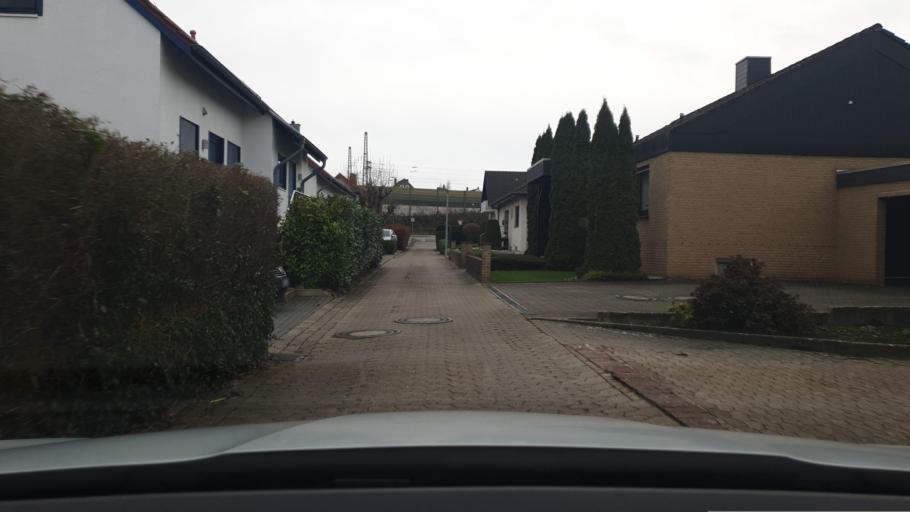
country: DE
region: North Rhine-Westphalia
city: Bad Oeynhausen
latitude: 52.2036
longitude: 8.7750
